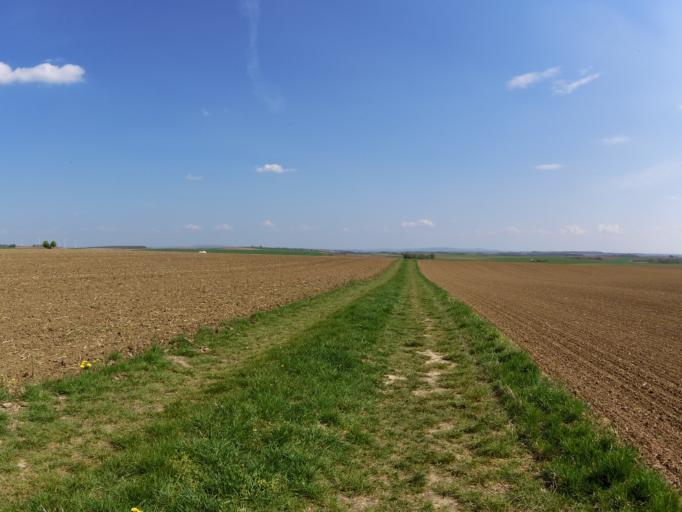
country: DE
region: Bavaria
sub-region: Regierungsbezirk Unterfranken
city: Giebelstadt
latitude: 49.6822
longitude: 9.9568
